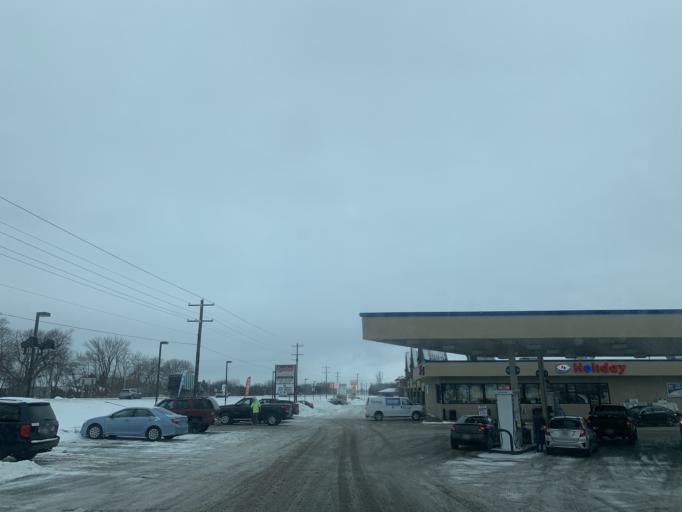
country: US
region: Wisconsin
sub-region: Saint Croix County
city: Hudson
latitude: 44.9678
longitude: -92.6794
